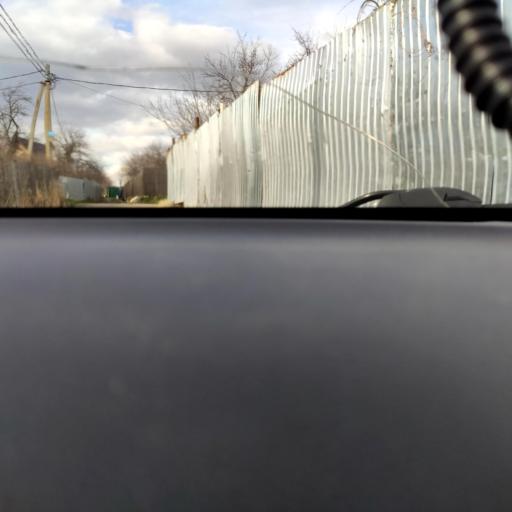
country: RU
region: Tatarstan
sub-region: Gorod Kazan'
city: Kazan
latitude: 55.8865
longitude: 49.0687
